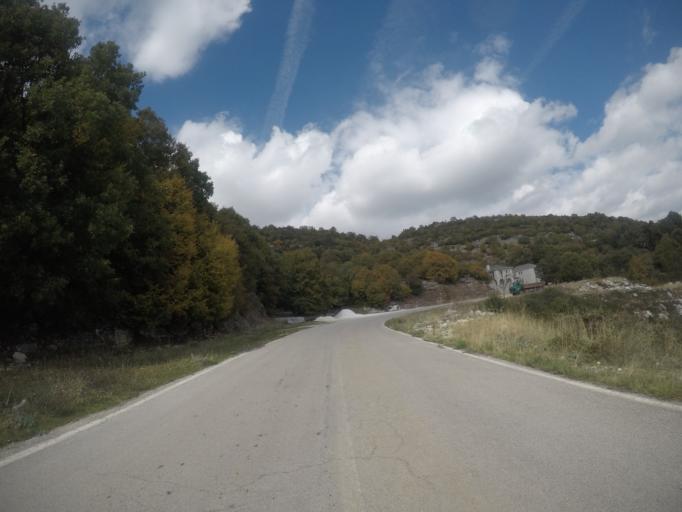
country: GR
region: Epirus
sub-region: Nomos Ioanninon
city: Asprangeloi
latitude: 39.8820
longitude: 20.7436
